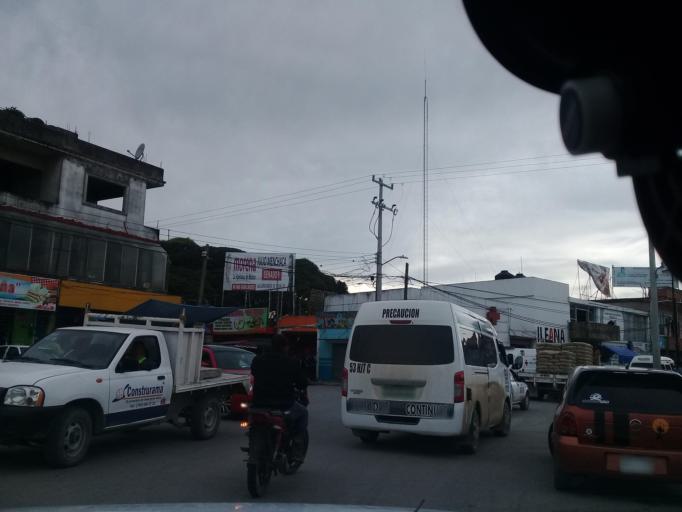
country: MX
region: Hidalgo
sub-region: Huejutla de Reyes
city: Huejutla de Reyes
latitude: 21.1432
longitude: -98.4160
